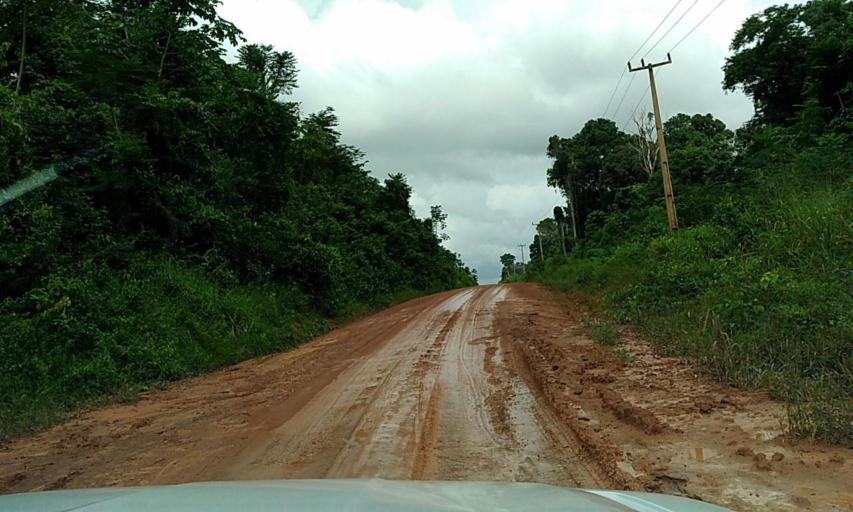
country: BR
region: Para
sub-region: Senador Jose Porfirio
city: Senador Jose Porfirio
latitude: -2.6762
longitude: -51.8340
